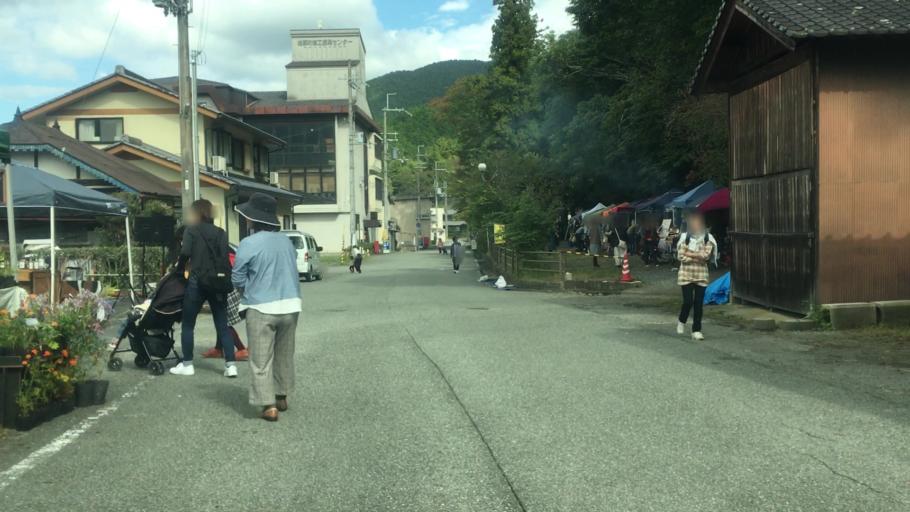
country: JP
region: Hyogo
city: Sasayama
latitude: 35.1308
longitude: 135.0784
